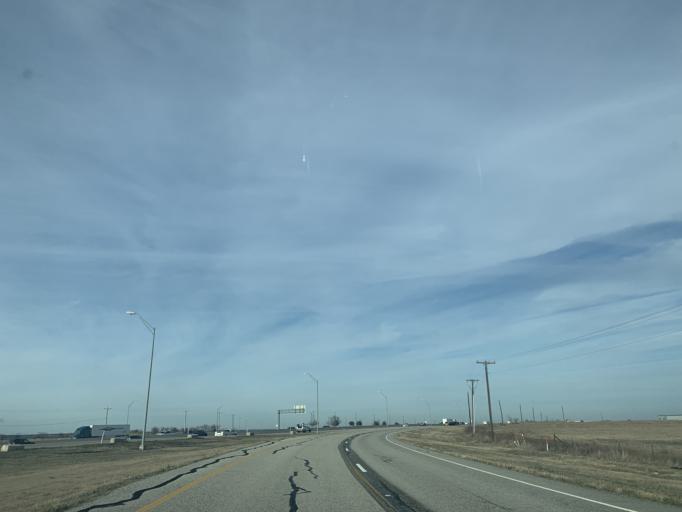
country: US
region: Texas
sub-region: Bell County
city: Salado
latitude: 30.9058
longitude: -97.5561
